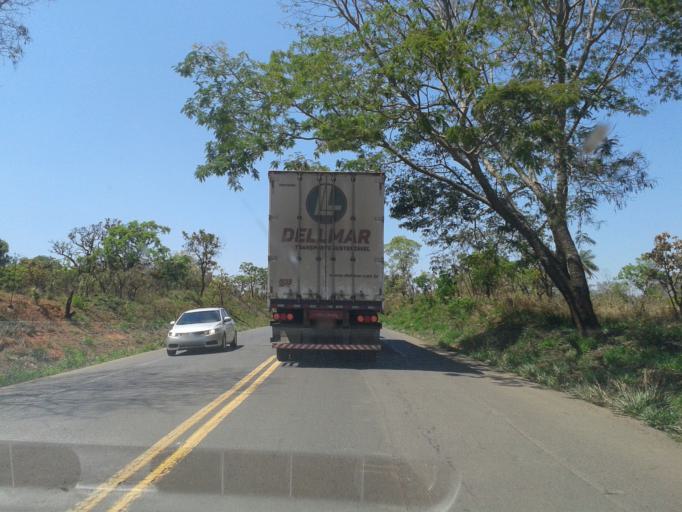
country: BR
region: Minas Gerais
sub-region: Araxa
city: Araxa
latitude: -19.4352
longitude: -47.1979
